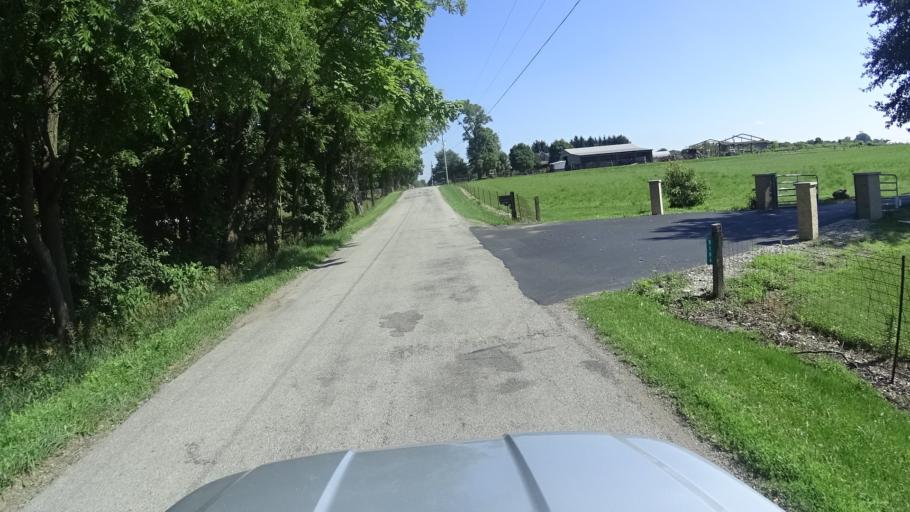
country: US
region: Indiana
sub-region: Madison County
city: Ingalls
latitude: 39.9706
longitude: -85.8150
